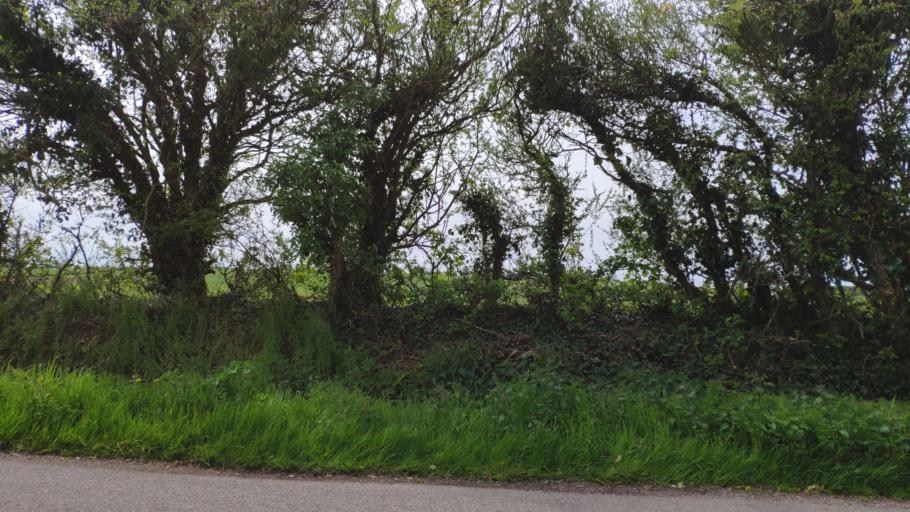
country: IE
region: Munster
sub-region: County Cork
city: Blarney
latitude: 51.9914
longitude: -8.5034
